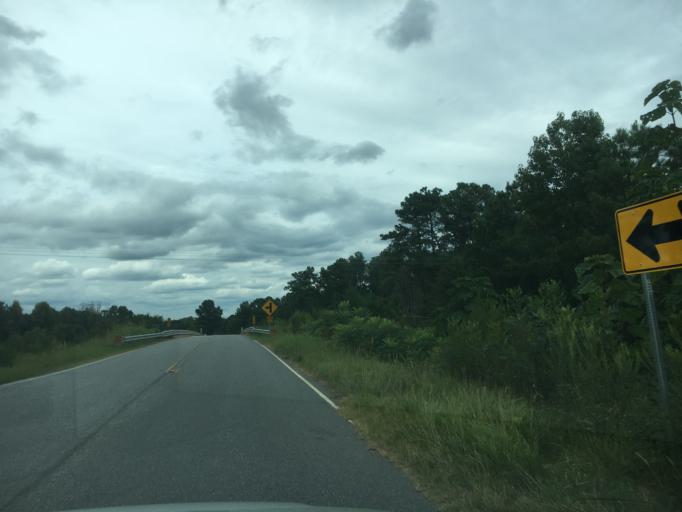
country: US
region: South Carolina
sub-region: Laurens County
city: Watts Mills
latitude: 34.5304
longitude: -81.9330
